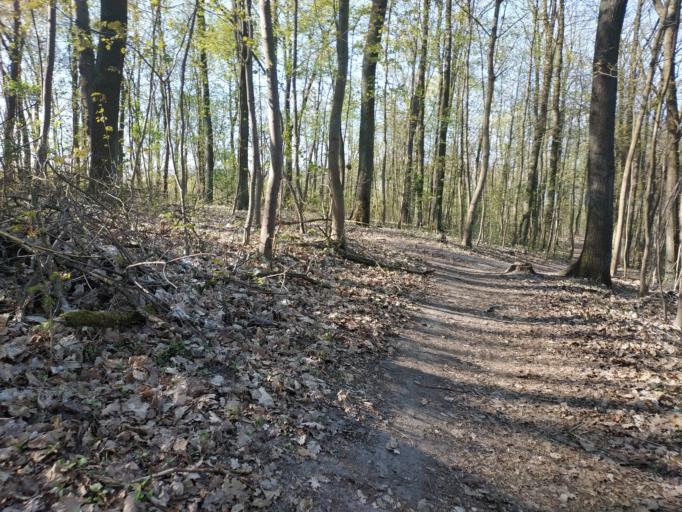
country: DE
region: Brandenburg
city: Petershagen
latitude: 52.5610
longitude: 13.8303
